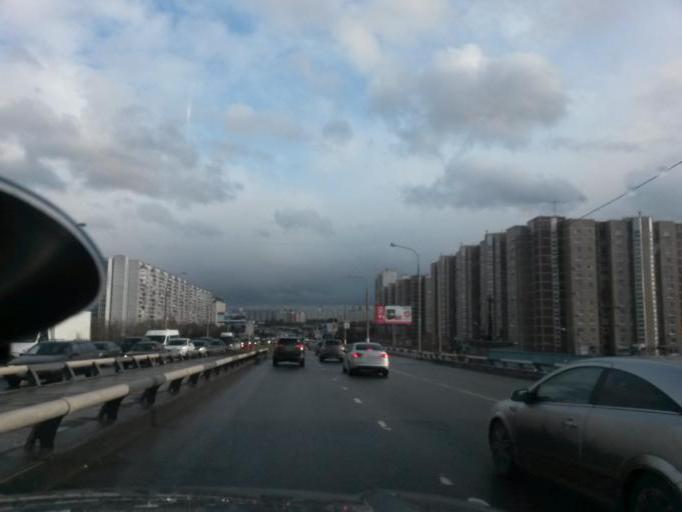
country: RU
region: Moscow
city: Brateyevo
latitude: 55.6381
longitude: 37.7485
